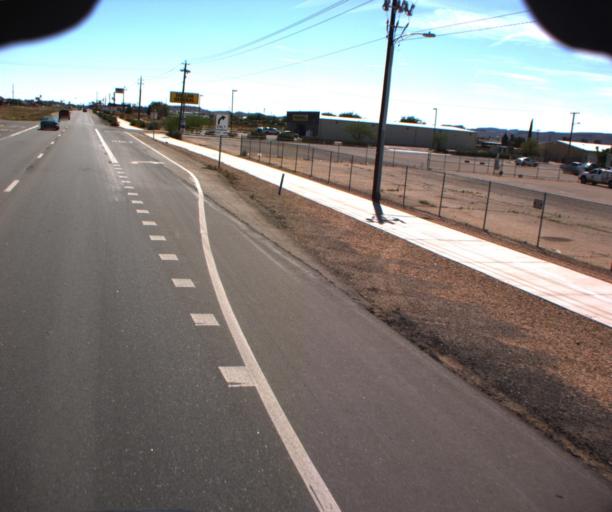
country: US
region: Arizona
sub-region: Mohave County
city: New Kingman-Butler
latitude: 35.2301
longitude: -113.9986
